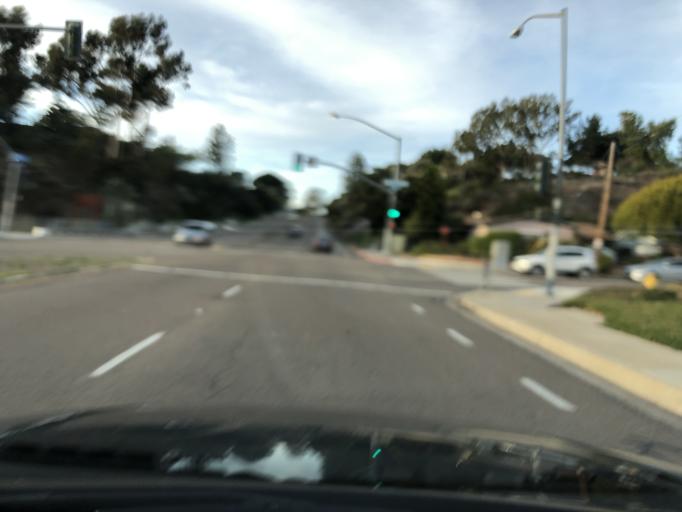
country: US
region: California
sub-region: San Diego County
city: La Jolla
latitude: 32.8284
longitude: -117.1929
